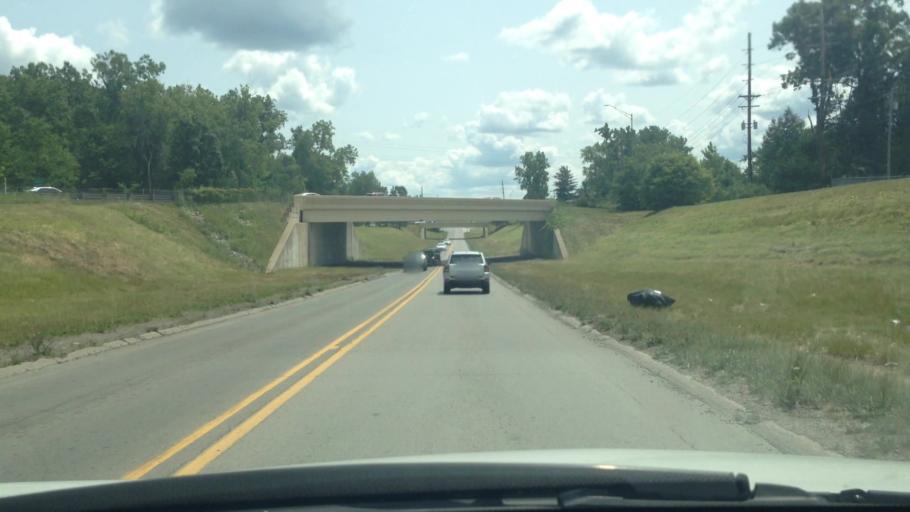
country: US
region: Michigan
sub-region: Wayne County
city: Taylor
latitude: 42.2507
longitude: -83.3085
